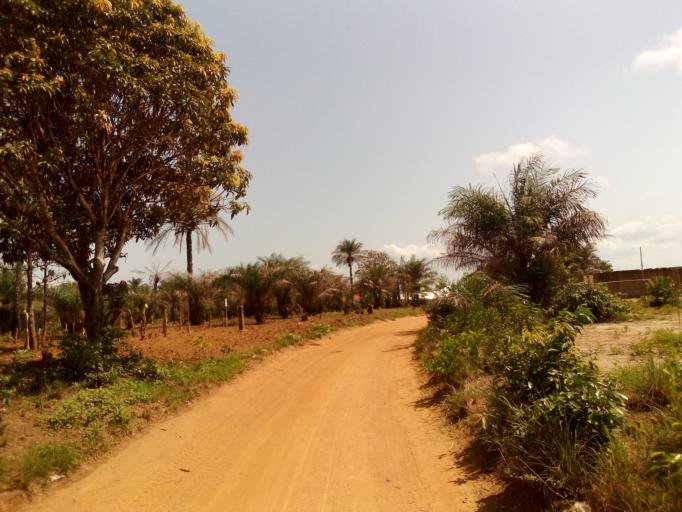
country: SL
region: Western Area
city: Waterloo
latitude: 8.3448
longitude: -13.0137
